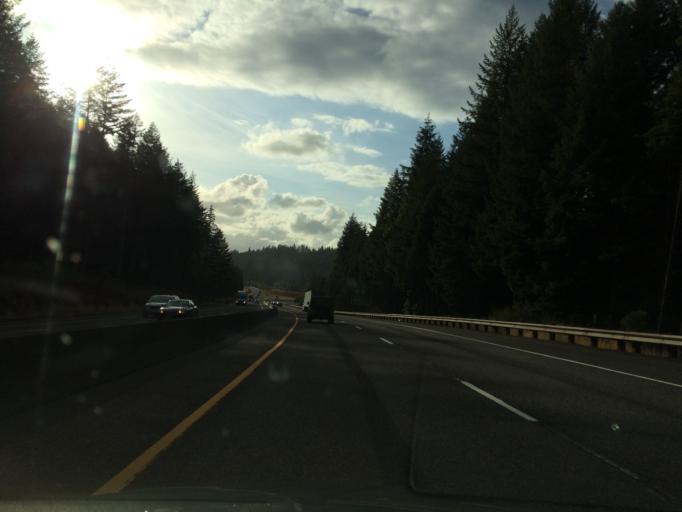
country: US
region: Oregon
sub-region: Douglas County
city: Drain
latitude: 43.7063
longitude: -123.2095
